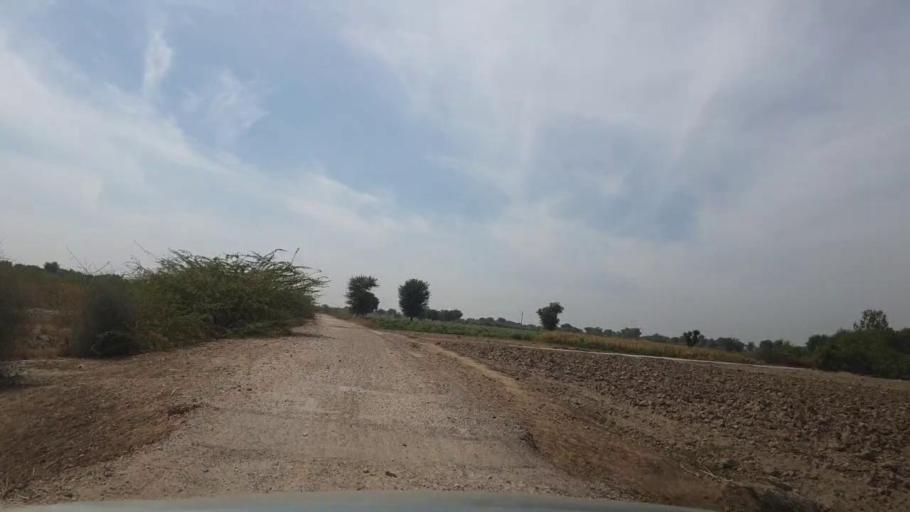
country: PK
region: Sindh
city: Nabisar
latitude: 25.1069
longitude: 69.6082
